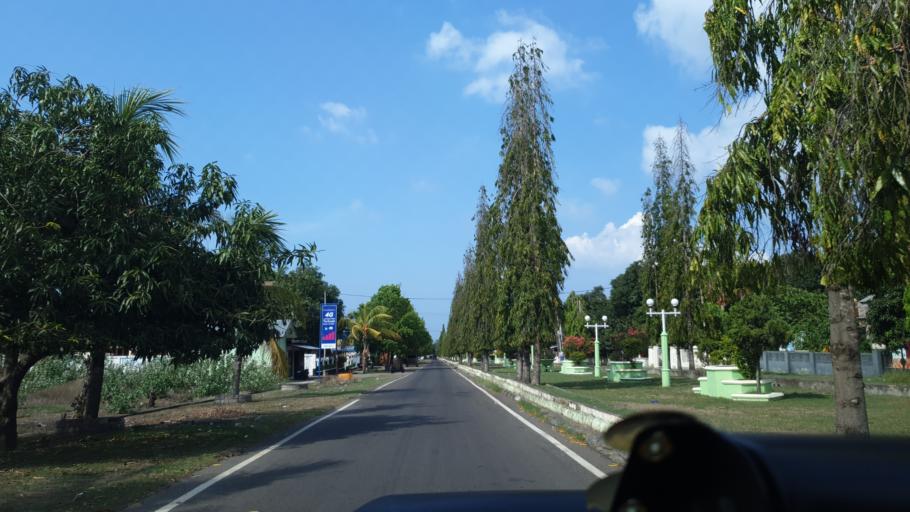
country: ID
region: East Nusa Tenggara
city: Waioti
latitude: -8.6336
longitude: 122.2359
